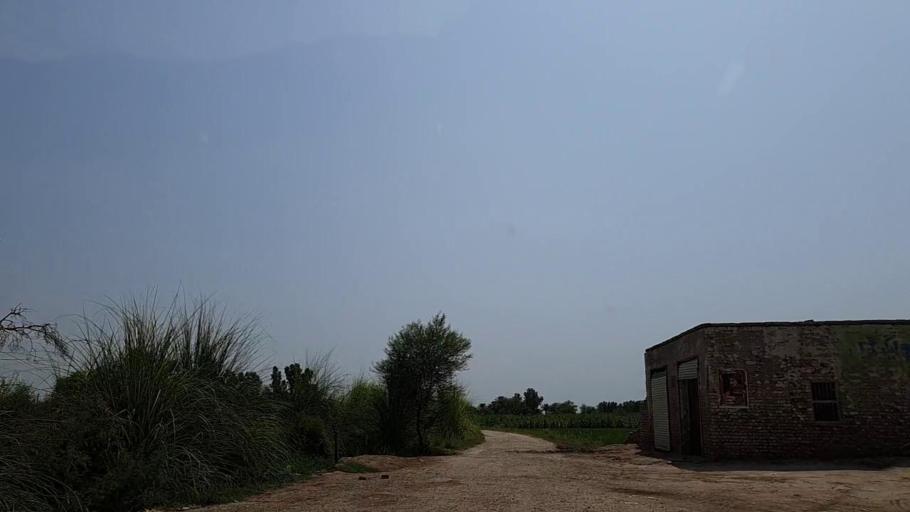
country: PK
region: Sindh
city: Adilpur
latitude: 27.9004
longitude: 69.3569
